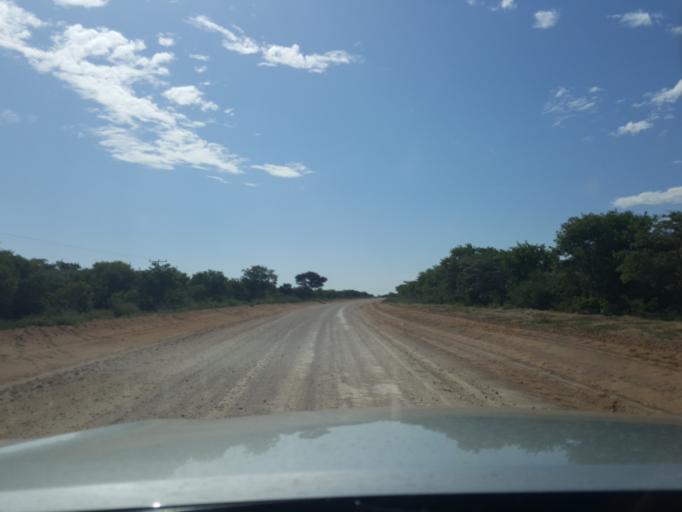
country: BW
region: Kweneng
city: Khudumelapye
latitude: -23.7920
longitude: 24.7897
